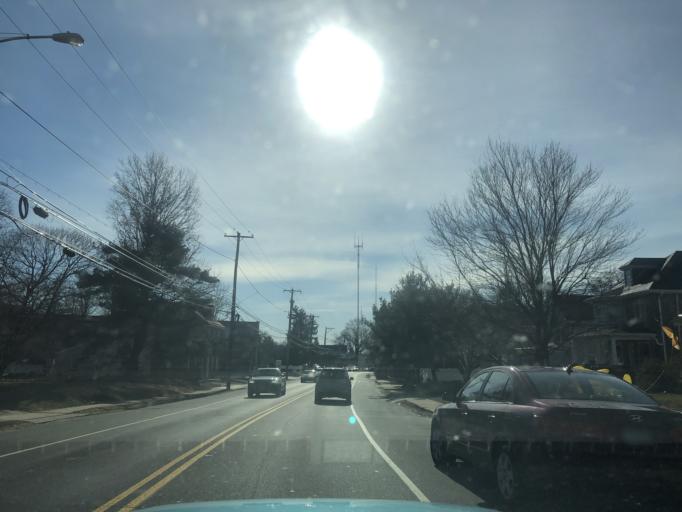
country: US
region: Pennsylvania
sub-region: Montgomery County
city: Bala-Cynwyd
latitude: 40.0561
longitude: -75.2360
